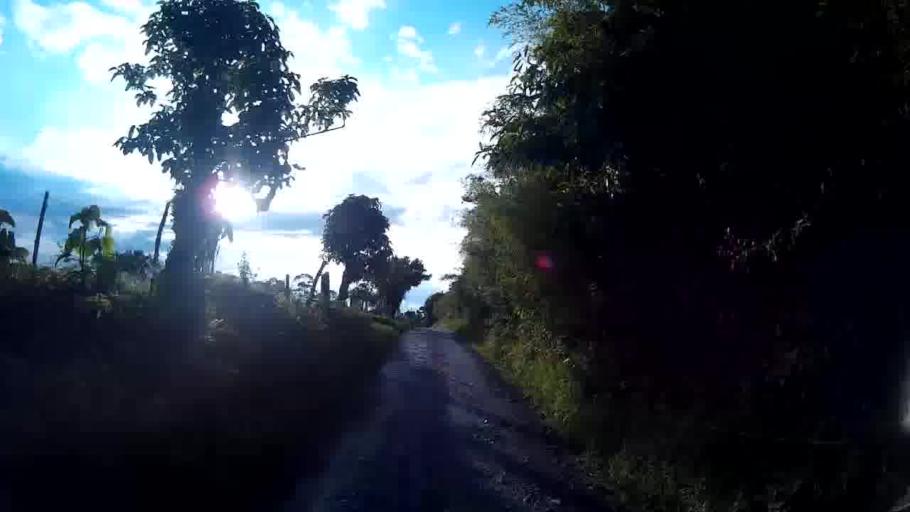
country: CO
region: Valle del Cauca
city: Ulloa
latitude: 4.7221
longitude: -75.6884
